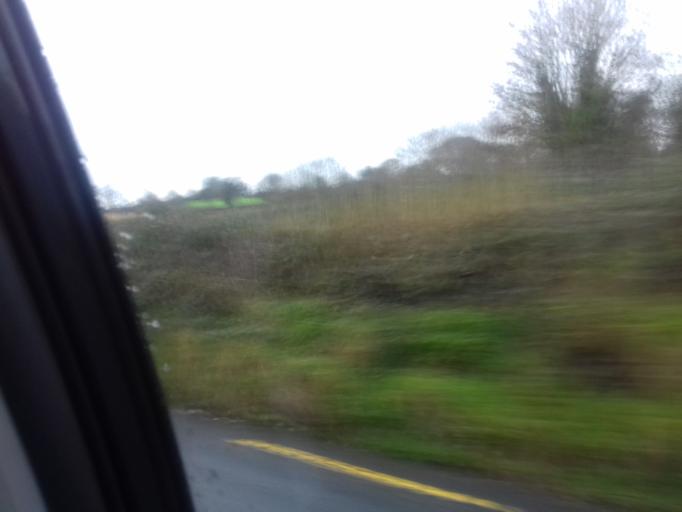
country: IE
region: Leinster
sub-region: Kilkenny
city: Graiguenamanagh
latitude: 52.5958
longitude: -6.9893
